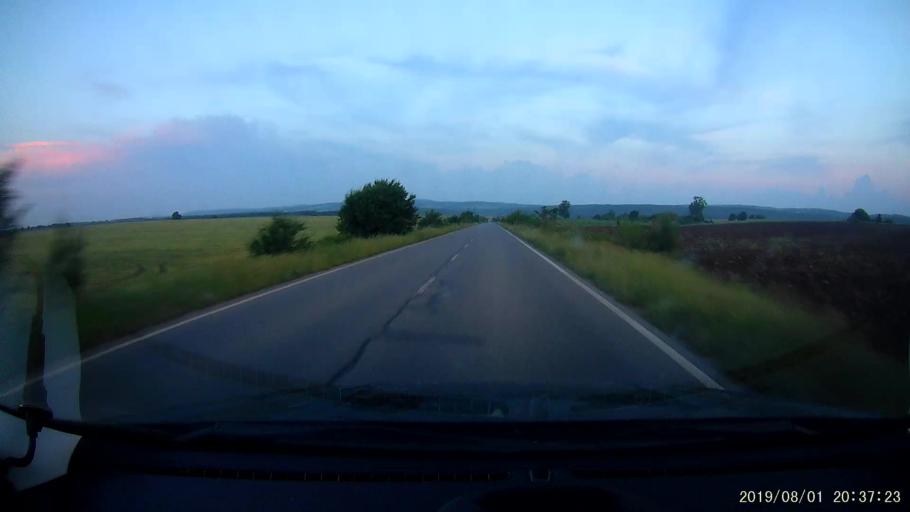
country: BG
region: Yambol
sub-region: Obshtina Elkhovo
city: Elkhovo
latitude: 42.0495
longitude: 26.5939
